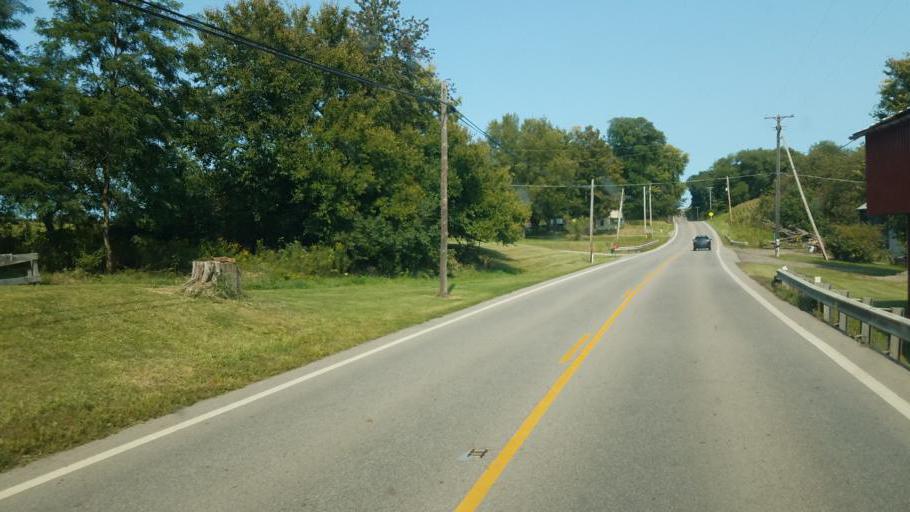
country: US
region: Ohio
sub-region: Wayne County
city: Shreve
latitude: 40.7369
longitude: -82.0311
